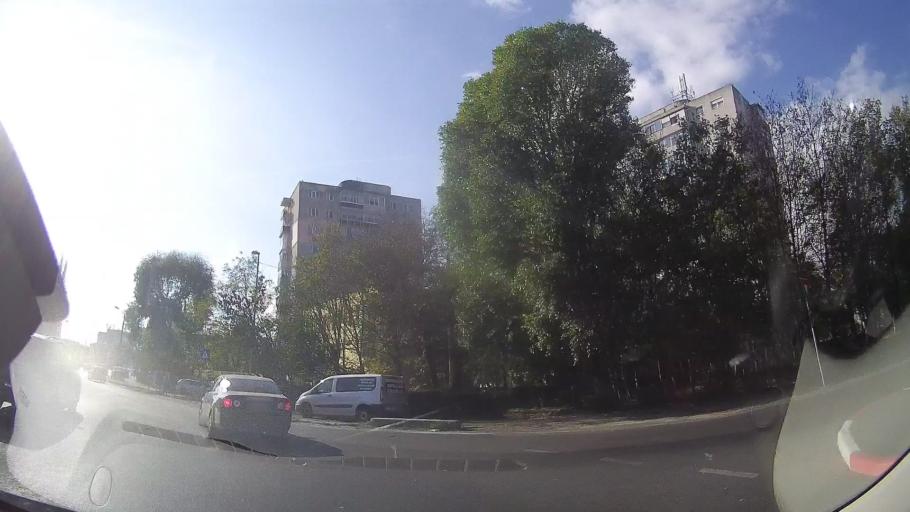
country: RO
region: Constanta
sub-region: Municipiul Constanta
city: Constanta
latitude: 44.1450
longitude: 28.6240
